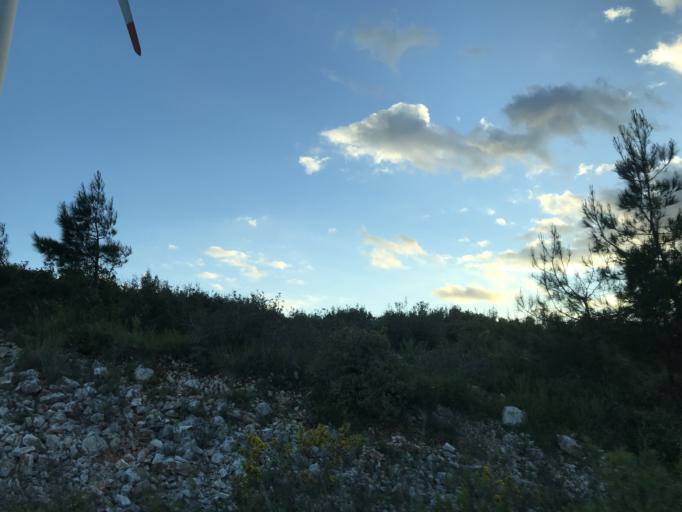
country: TR
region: Hatay
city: Buyukcat
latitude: 36.0948
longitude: 36.0378
